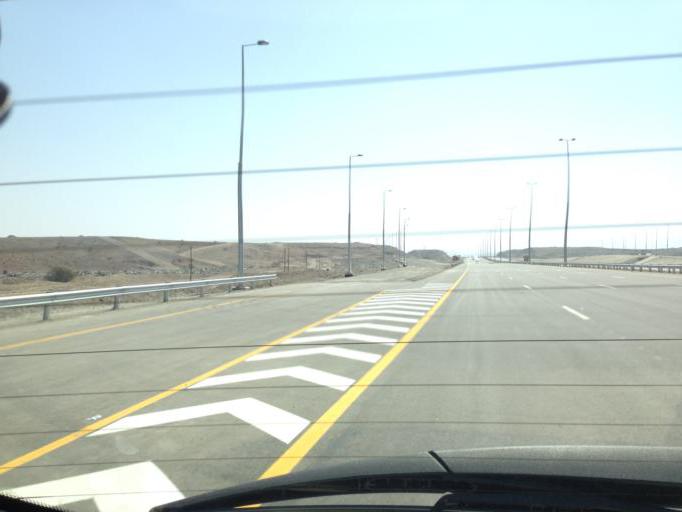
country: OM
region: Al Batinah
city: Rustaq
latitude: 23.5507
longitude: 57.5078
